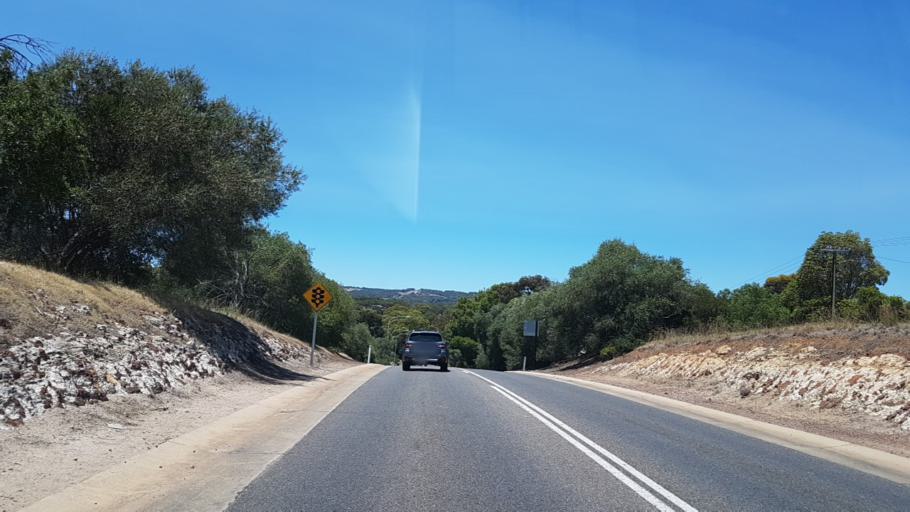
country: AU
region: South Australia
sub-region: Marion
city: Trott Park
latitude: -35.0827
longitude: 138.5565
